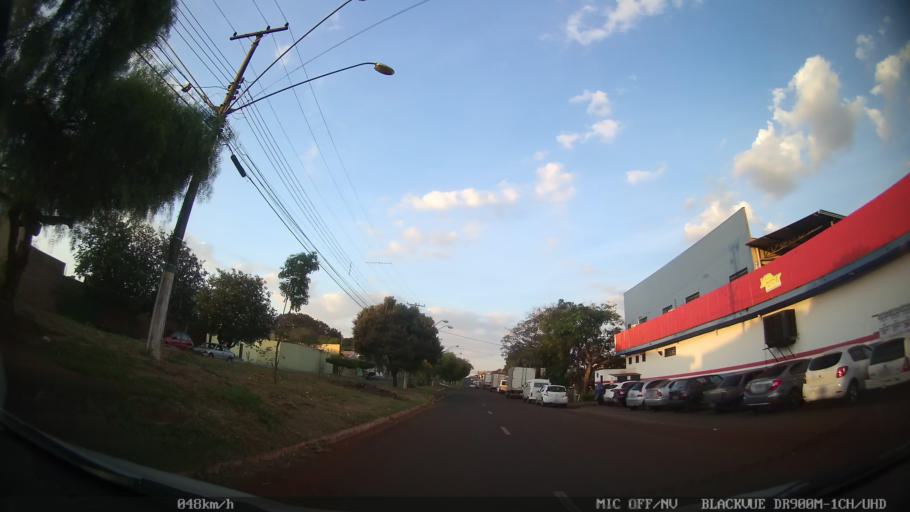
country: BR
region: Sao Paulo
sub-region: Ribeirao Preto
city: Ribeirao Preto
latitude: -21.1392
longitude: -47.8520
